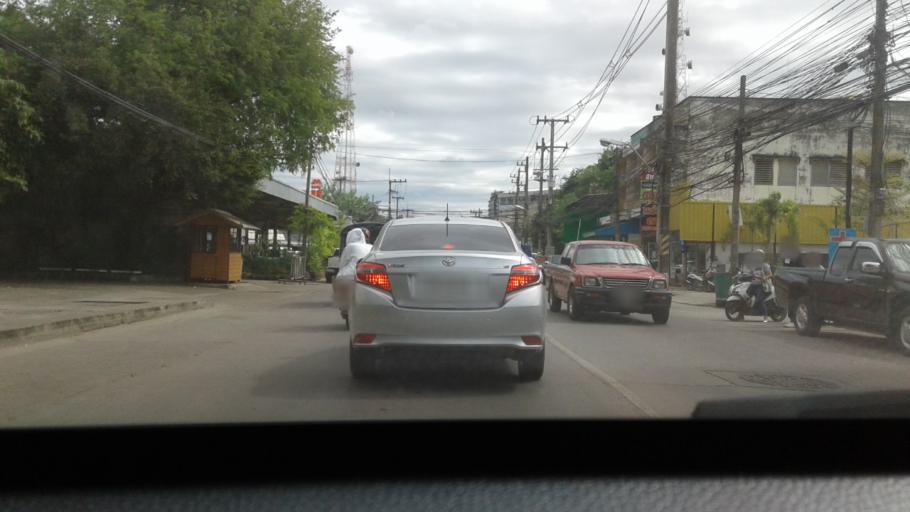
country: TH
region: Changwat Udon Thani
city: Udon Thani
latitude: 17.4140
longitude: 102.7909
